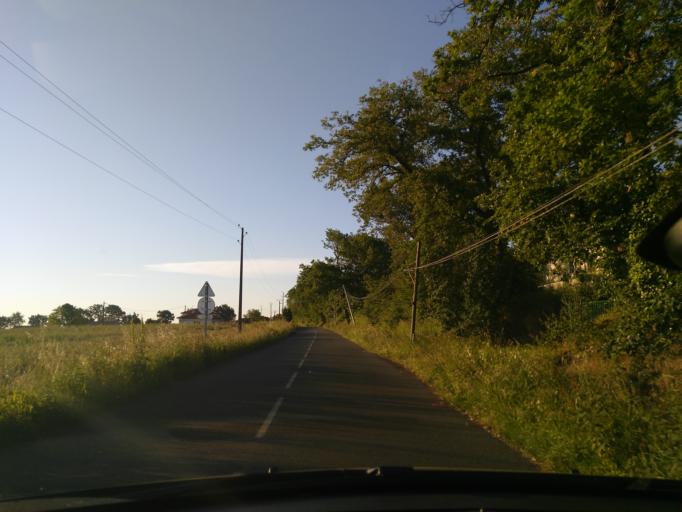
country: FR
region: Midi-Pyrenees
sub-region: Departement de la Haute-Garonne
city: Merville
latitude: 43.7287
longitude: 1.2951
